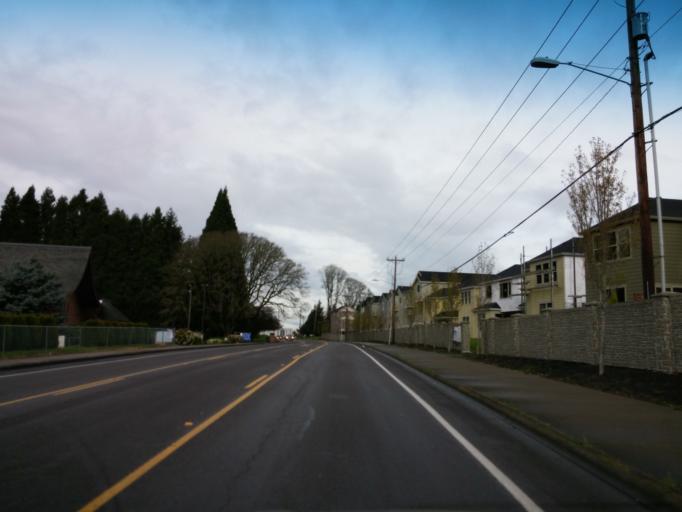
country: US
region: Oregon
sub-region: Washington County
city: Oak Hills
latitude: 45.5346
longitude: -122.8432
